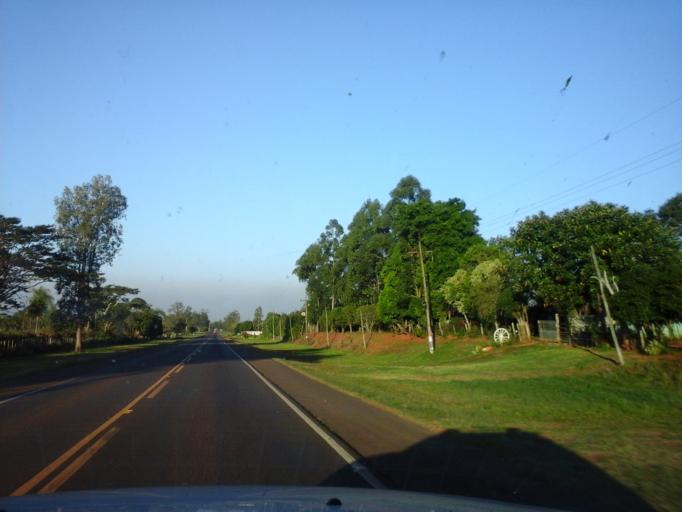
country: PY
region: Itapua
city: General Delgado
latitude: -27.0848
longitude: -56.5472
